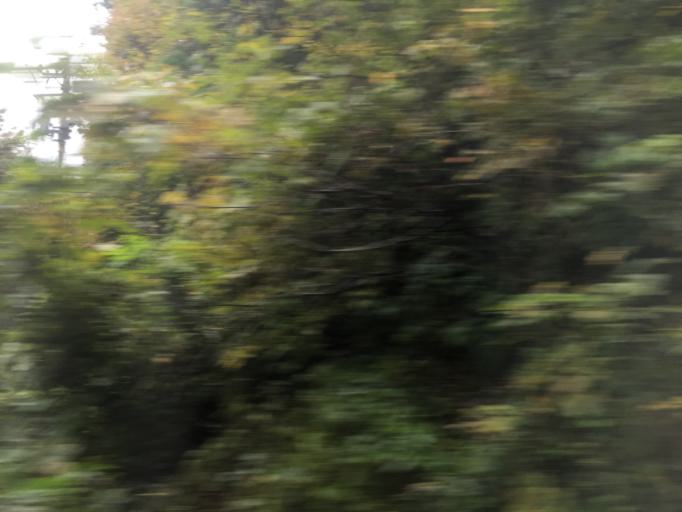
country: JP
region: Niigata
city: Murakami
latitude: 38.0793
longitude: 139.6589
